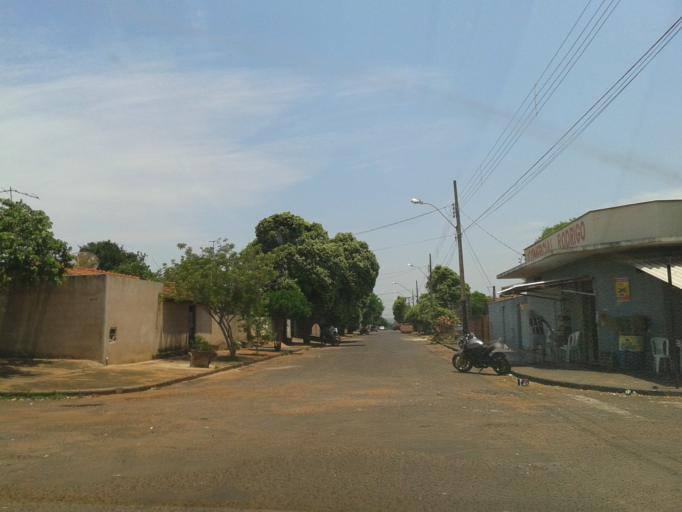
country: BR
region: Minas Gerais
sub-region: Ituiutaba
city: Ituiutaba
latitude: -18.9890
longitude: -49.4453
